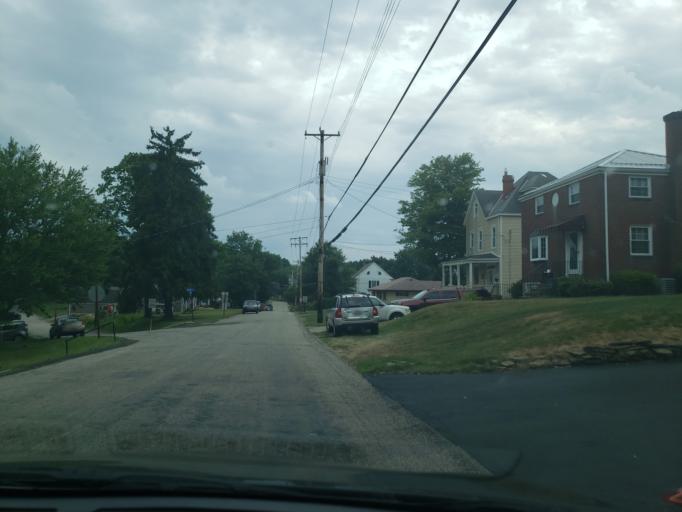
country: US
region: Pennsylvania
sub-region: Allegheny County
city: Avalon
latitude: 40.5111
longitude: -80.0703
